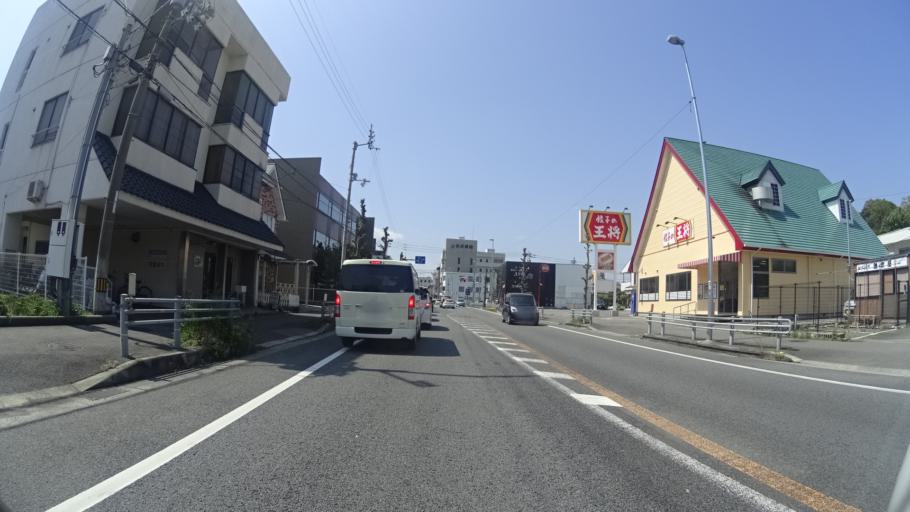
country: JP
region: Tokushima
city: Narutocho-mitsuishi
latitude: 34.1812
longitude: 134.6100
